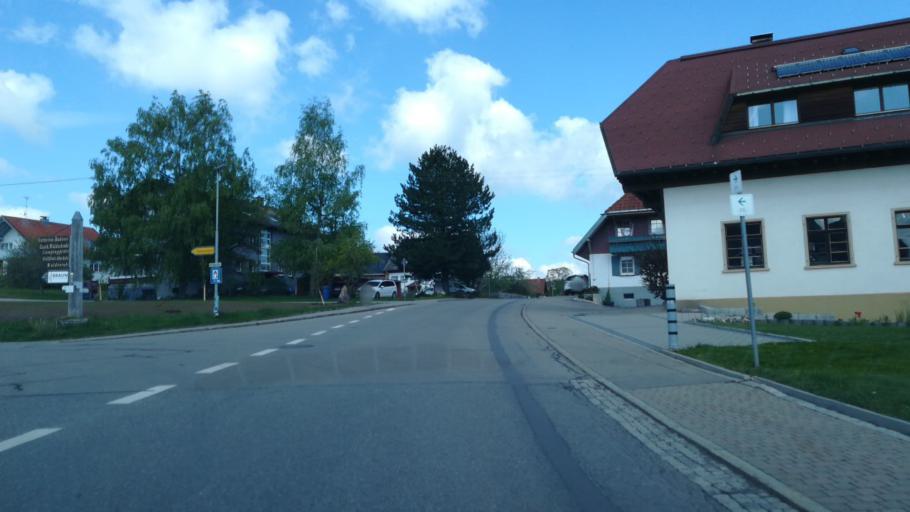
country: DE
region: Baden-Wuerttemberg
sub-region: Freiburg Region
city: Uhlingen-Birkendorf
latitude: 47.7503
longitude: 8.3115
